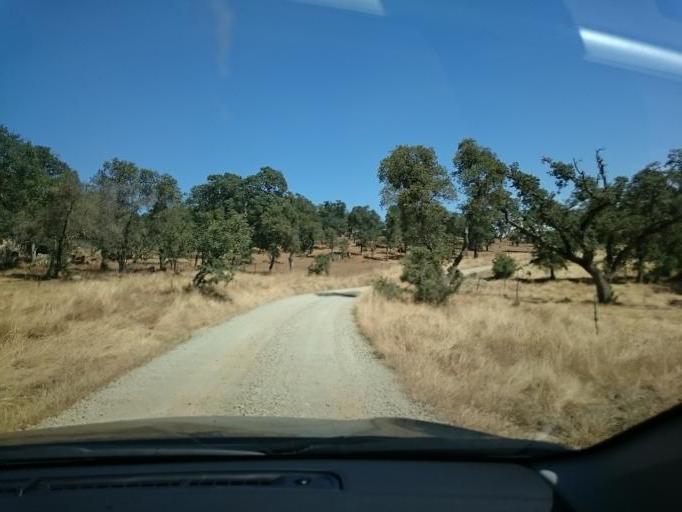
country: US
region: California
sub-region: Calaveras County
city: Rancho Calaveras
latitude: 38.0975
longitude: -120.7623
